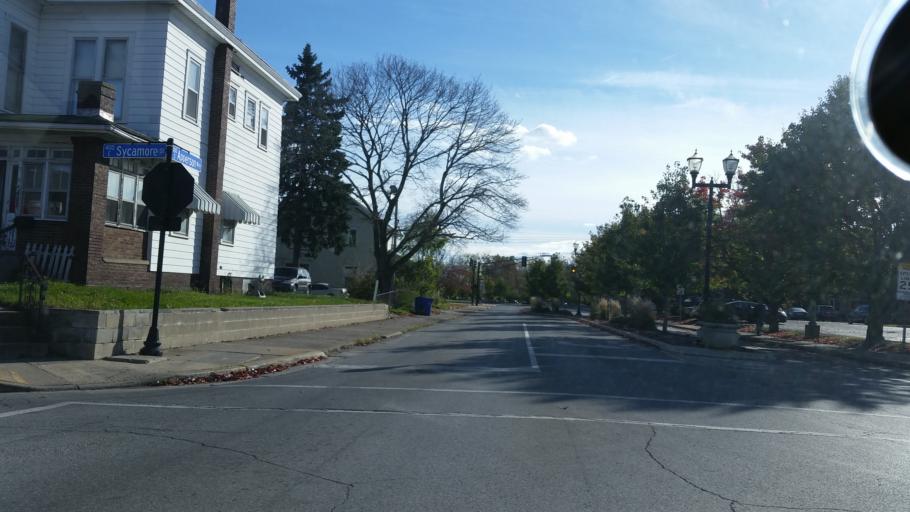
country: US
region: Indiana
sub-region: Howard County
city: Kokomo
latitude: 40.4865
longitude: -86.1275
